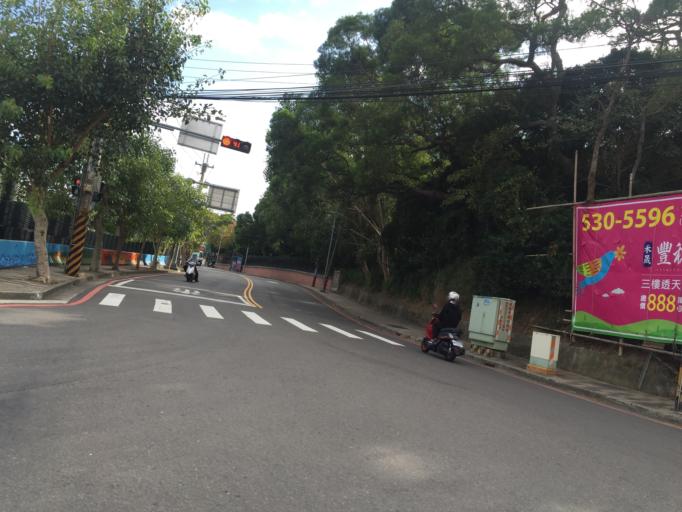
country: TW
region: Taiwan
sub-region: Hsinchu
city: Hsinchu
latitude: 24.7761
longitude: 120.9439
